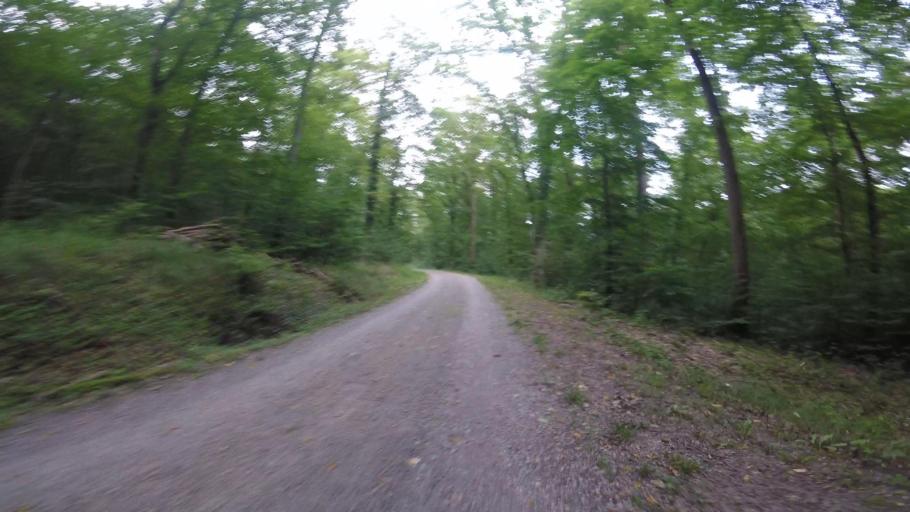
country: DE
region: Baden-Wuerttemberg
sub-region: Regierungsbezirk Stuttgart
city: Oberstenfeld
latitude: 48.9873
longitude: 9.3342
